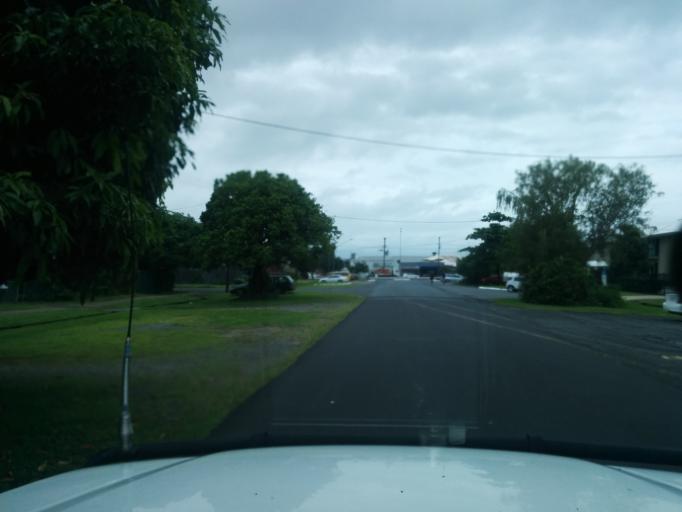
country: AU
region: Queensland
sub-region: Cairns
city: Cairns
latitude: -16.9303
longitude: 145.7565
